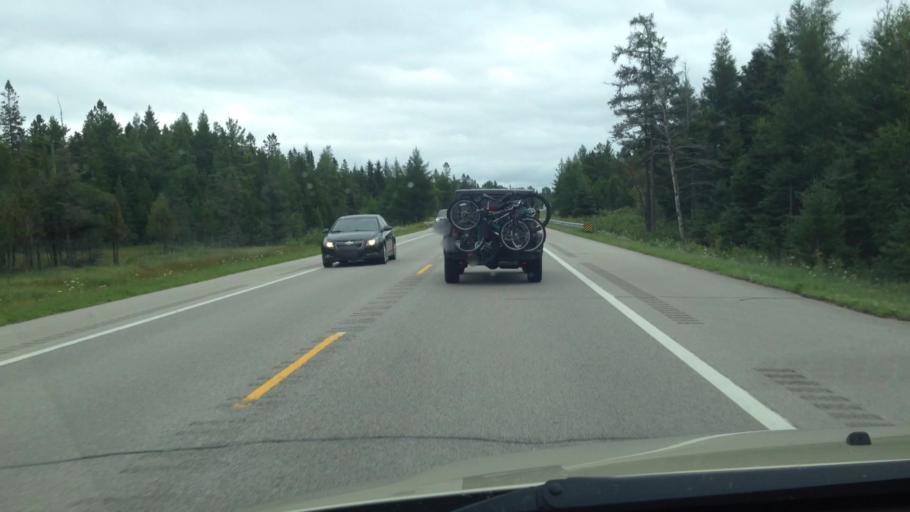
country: US
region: Michigan
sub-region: Luce County
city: Newberry
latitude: 46.0745
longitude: -85.2848
